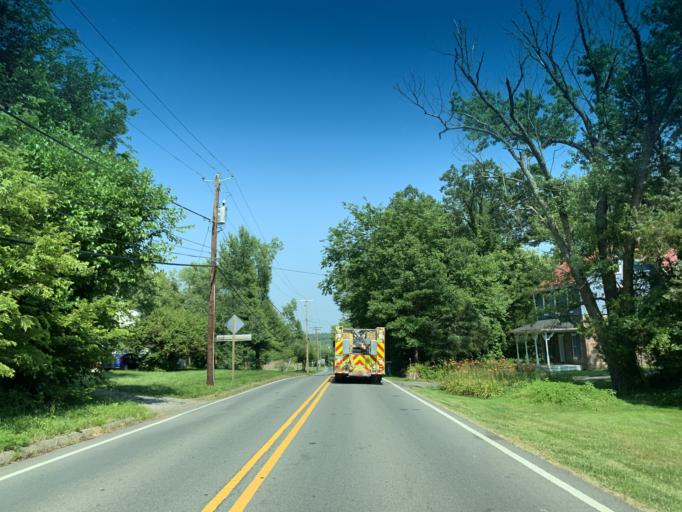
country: US
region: Maryland
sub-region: Montgomery County
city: Darnestown
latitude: 39.1284
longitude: -77.3454
